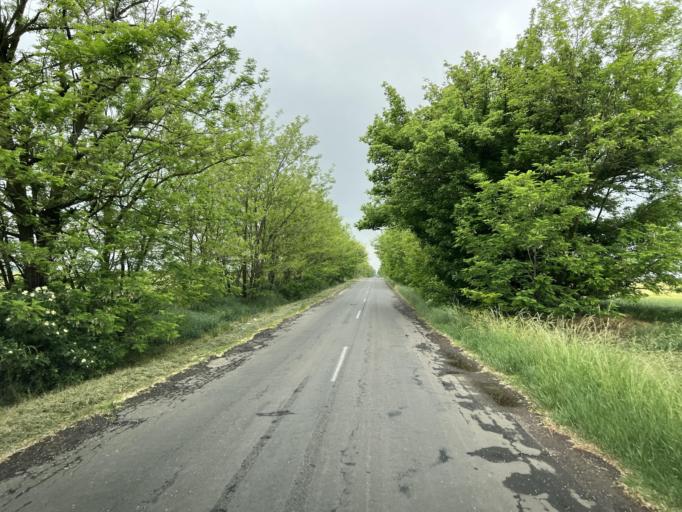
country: HU
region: Pest
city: Tura
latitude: 47.6183
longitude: 19.6366
